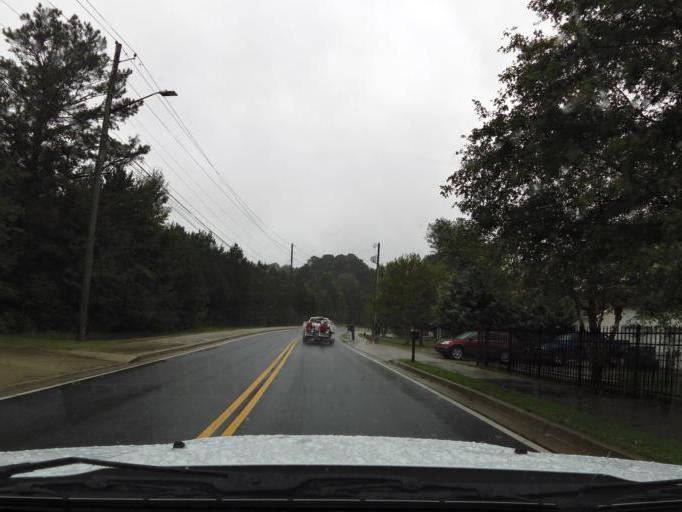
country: US
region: Georgia
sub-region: Cobb County
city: Acworth
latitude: 34.0438
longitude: -84.6706
